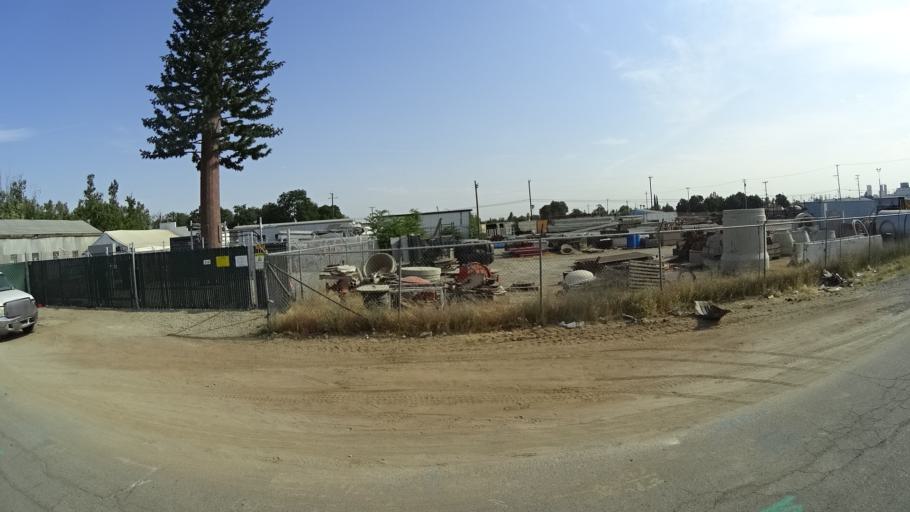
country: US
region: California
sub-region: Fresno County
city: Fresno
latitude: 36.7476
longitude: -119.8146
